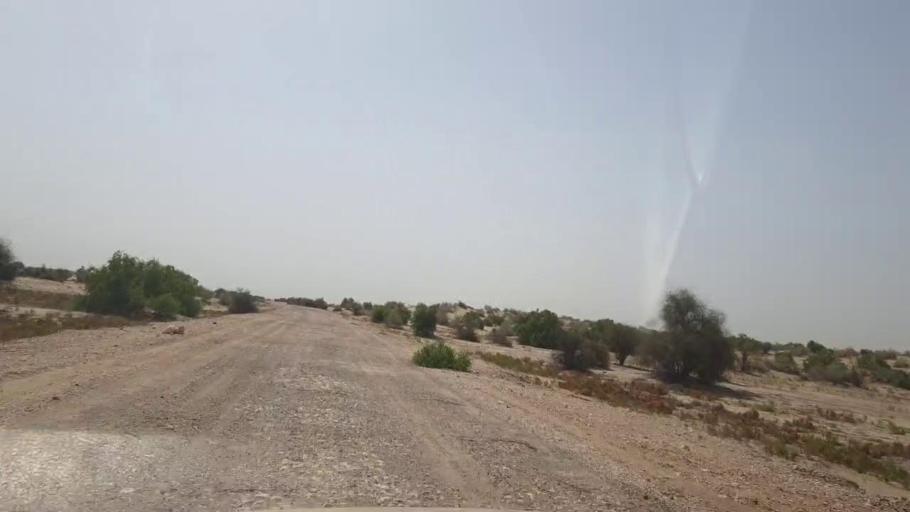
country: PK
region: Sindh
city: Rohri
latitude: 27.4360
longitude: 69.2466
